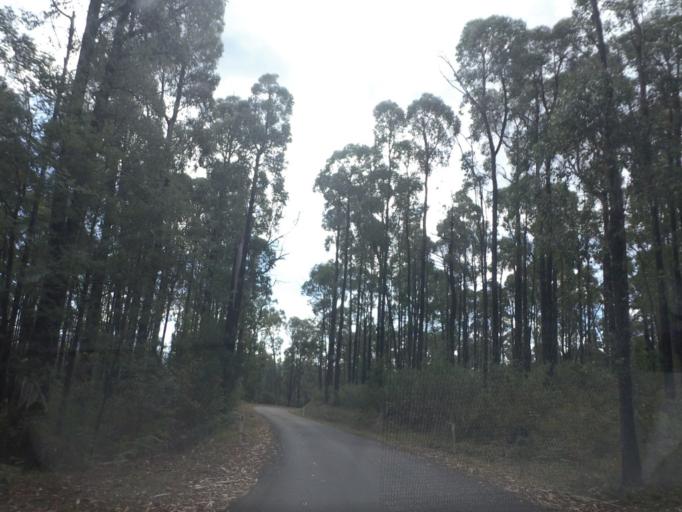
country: AU
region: Victoria
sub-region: Yarra Ranges
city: Healesville
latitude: -37.5570
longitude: 145.6759
